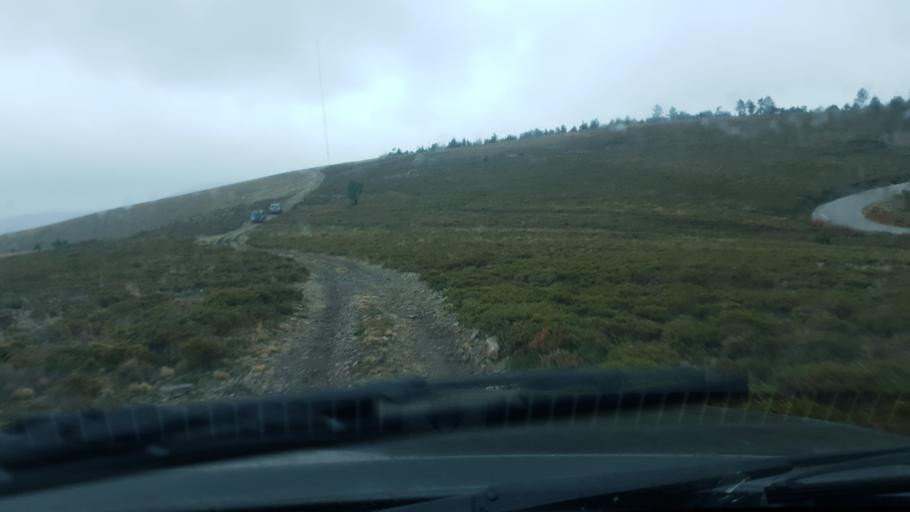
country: PT
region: Viseu
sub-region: Sao Pedro do Sul
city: Sao Pedro do Sul
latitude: 40.8635
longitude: -8.0937
